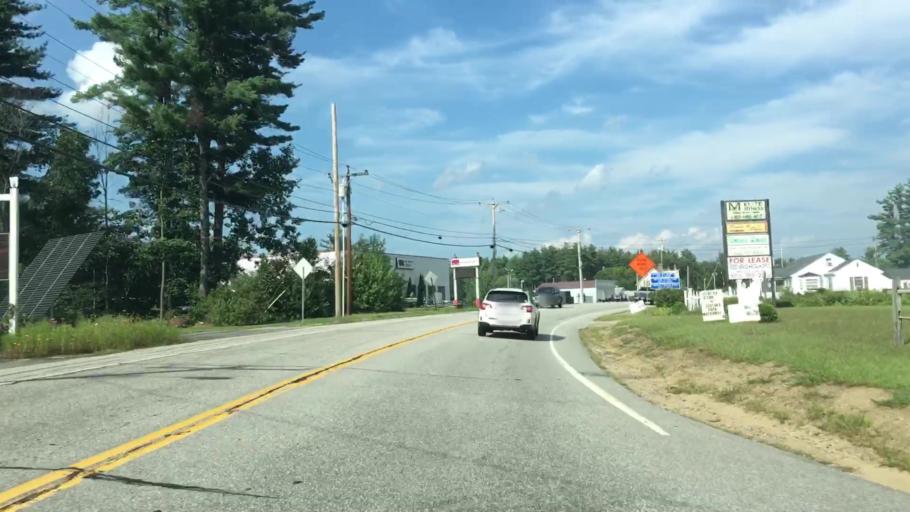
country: US
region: New Hampshire
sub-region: Belknap County
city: Laconia
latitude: 43.4991
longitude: -71.5184
